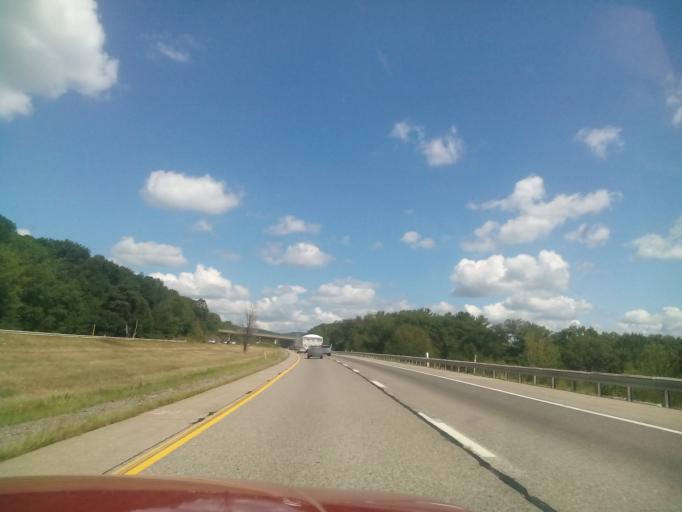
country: US
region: Pennsylvania
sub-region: Luzerne County
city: Conyngham
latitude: 41.0068
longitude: -76.1378
